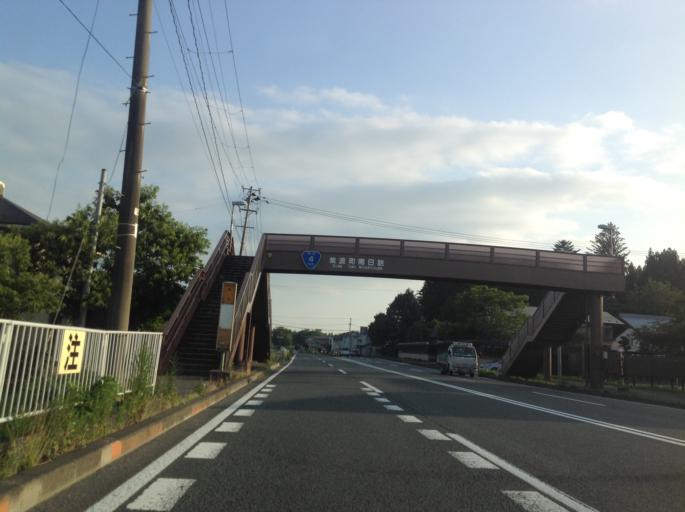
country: JP
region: Iwate
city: Hanamaki
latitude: 39.5356
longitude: 141.1668
